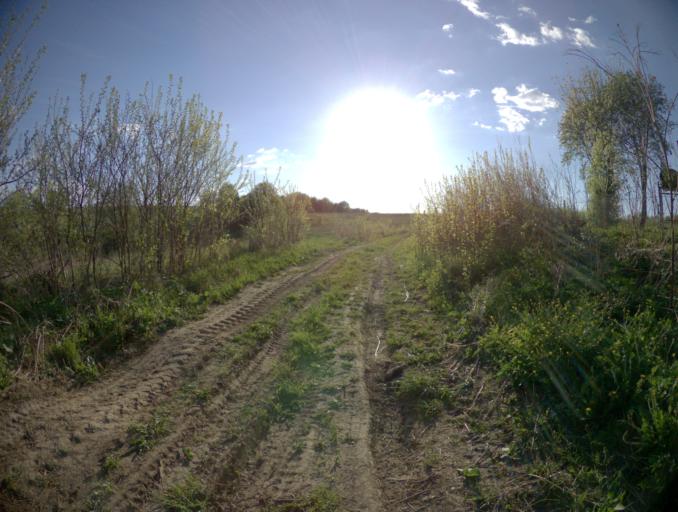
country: RU
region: Ivanovo
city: Gavrilov Posad
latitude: 56.3810
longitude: 40.1337
